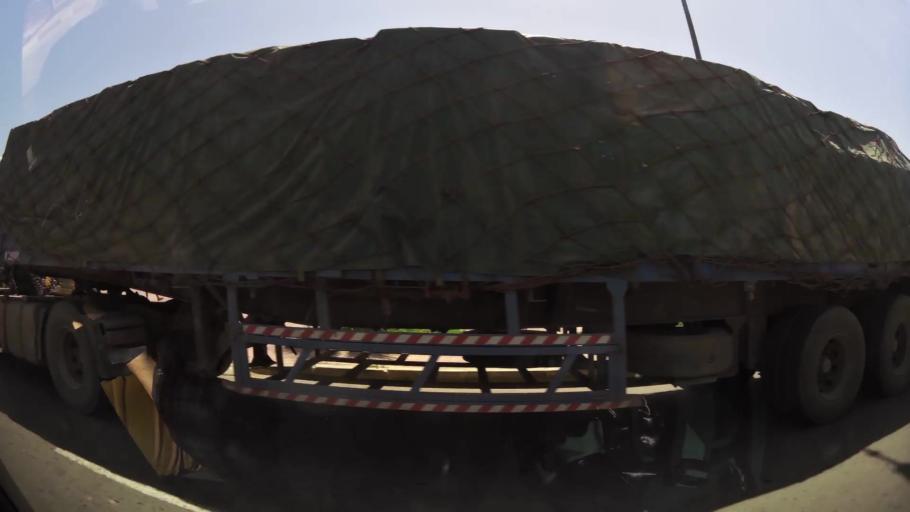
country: MA
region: Souss-Massa-Draa
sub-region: Inezgane-Ait Mellou
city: Inezgane
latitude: 30.3503
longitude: -9.4973
